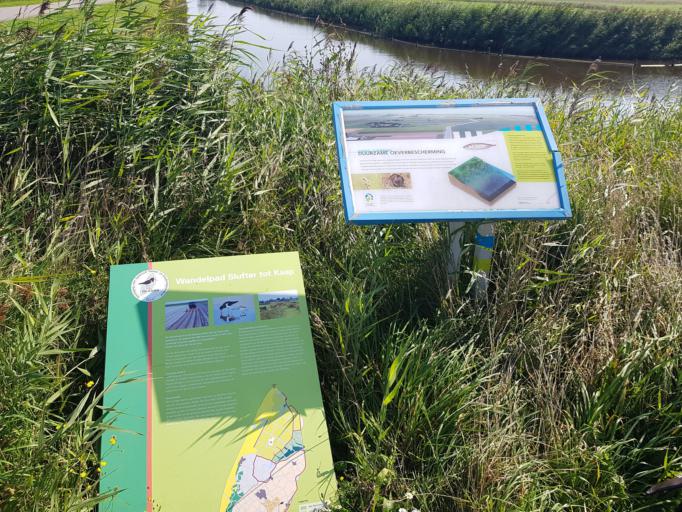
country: NL
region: North Holland
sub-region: Gemeente Texel
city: Den Burg
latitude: 53.1006
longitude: 4.8764
